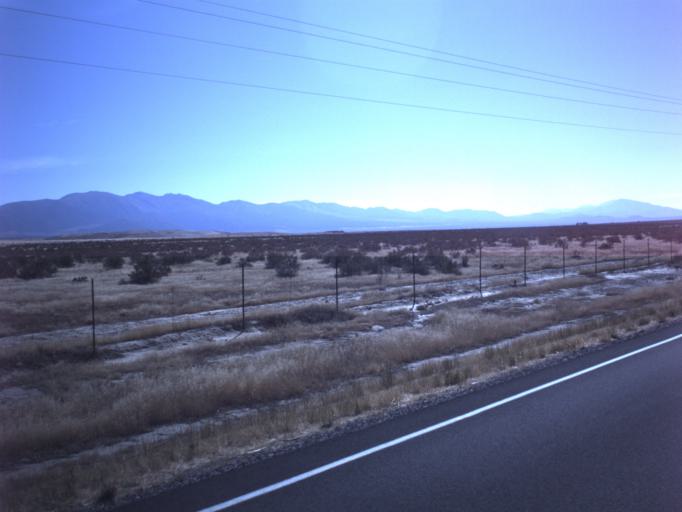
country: US
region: Utah
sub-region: Tooele County
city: Grantsville
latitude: 40.3725
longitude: -112.7465
